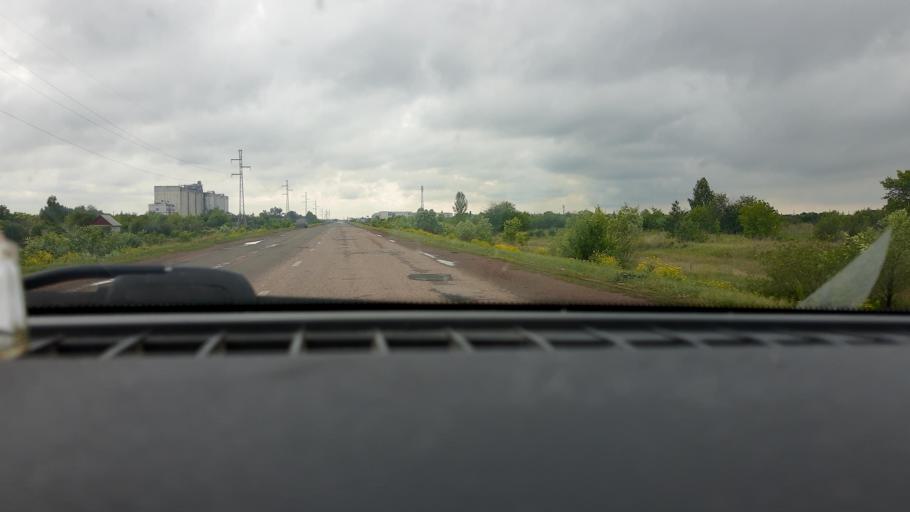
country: RU
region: Bashkortostan
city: Priyutovo
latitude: 53.9140
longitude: 53.9509
